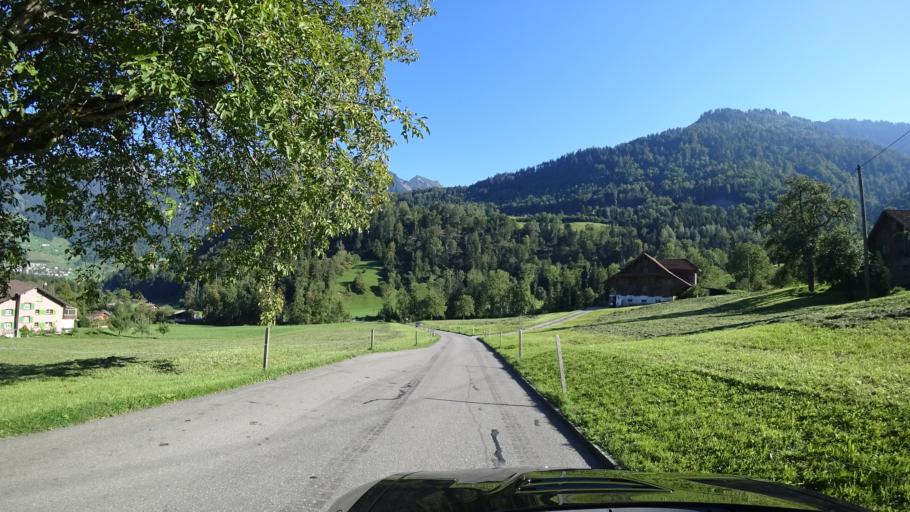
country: CH
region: Obwalden
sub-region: Obwalden
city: Giswil
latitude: 46.8304
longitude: 8.1542
